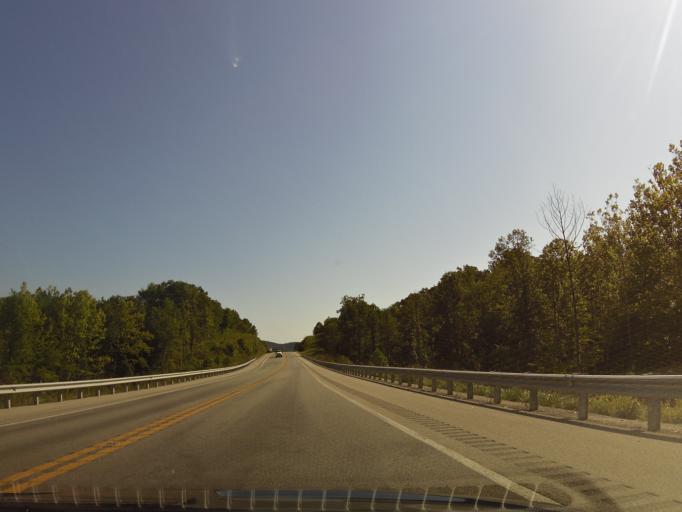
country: US
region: Kentucky
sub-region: Laurel County
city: London
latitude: 37.1100
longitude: -83.9362
